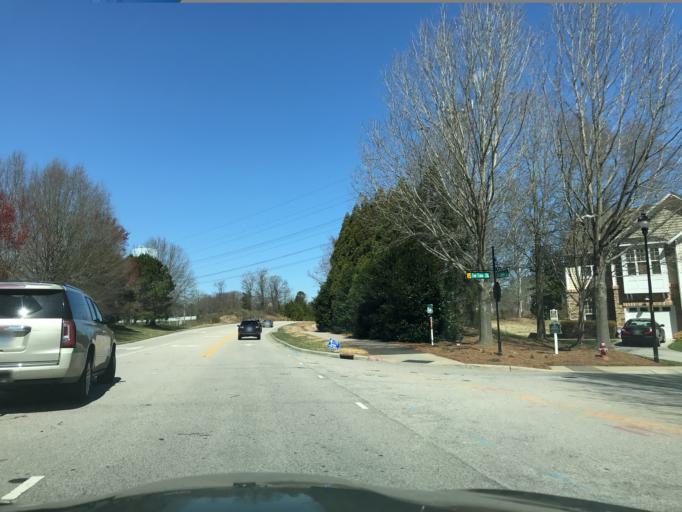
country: US
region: North Carolina
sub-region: Wake County
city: Wake Forest
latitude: 35.9629
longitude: -78.5628
